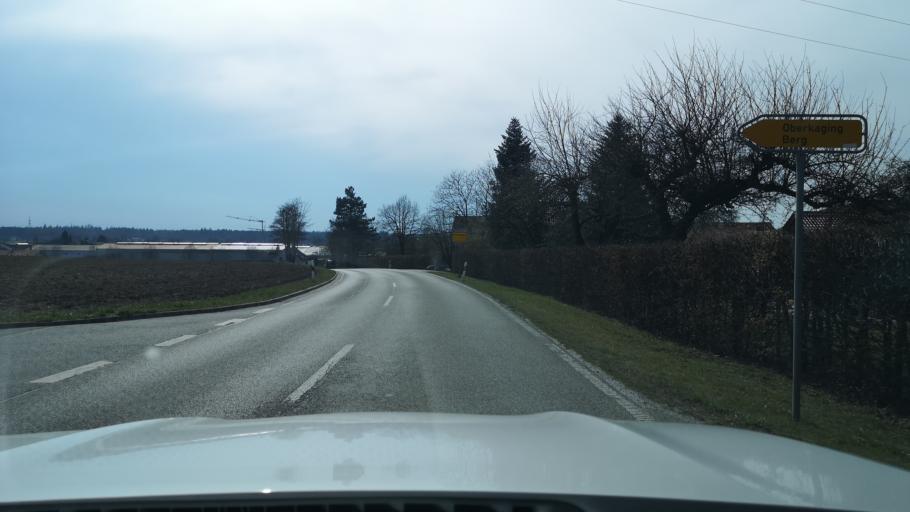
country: DE
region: Bavaria
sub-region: Upper Bavaria
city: Hohenlinden
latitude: 48.1590
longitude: 12.0061
